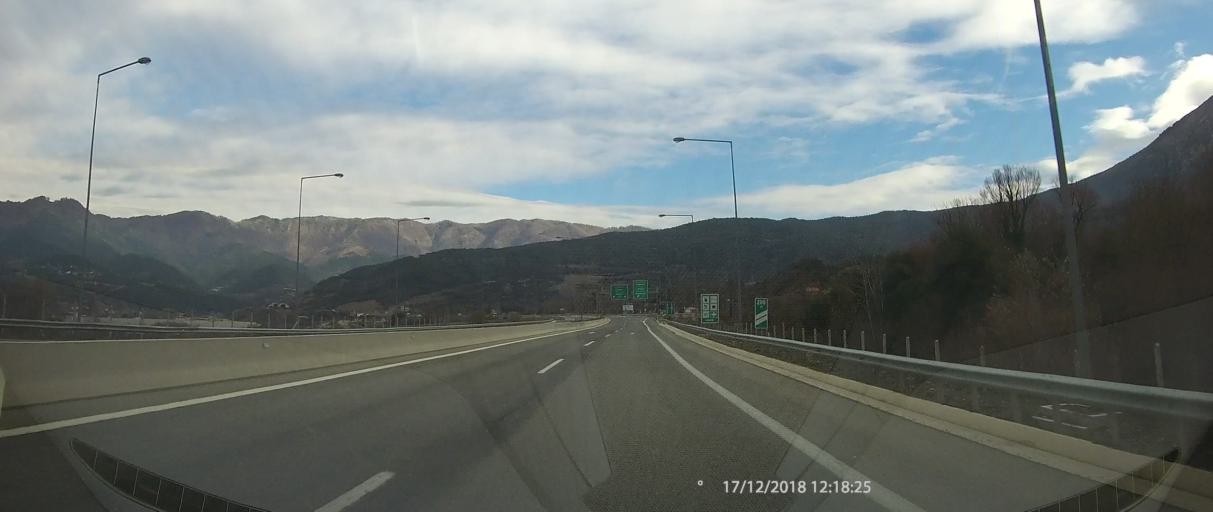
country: GR
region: Epirus
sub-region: Nomos Ioanninon
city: Metsovo
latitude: 39.7526
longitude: 21.0836
